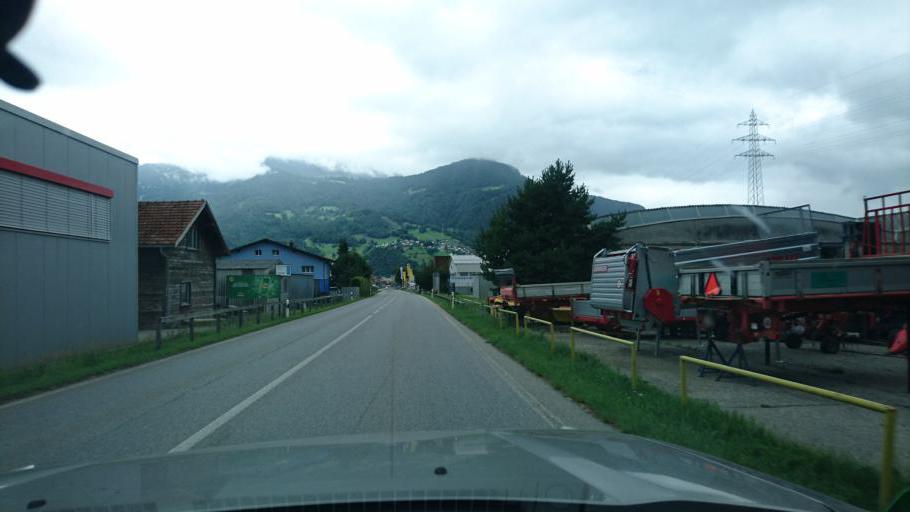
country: CH
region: Grisons
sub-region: Landquart District
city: Malans
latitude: 46.9688
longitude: 9.5757
